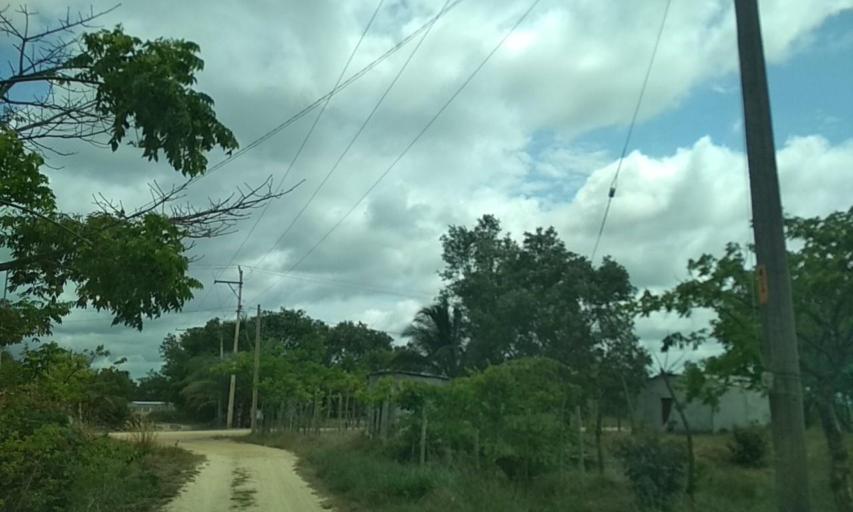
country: MX
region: Veracruz
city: Las Choapas
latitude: 17.8989
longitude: -94.1188
